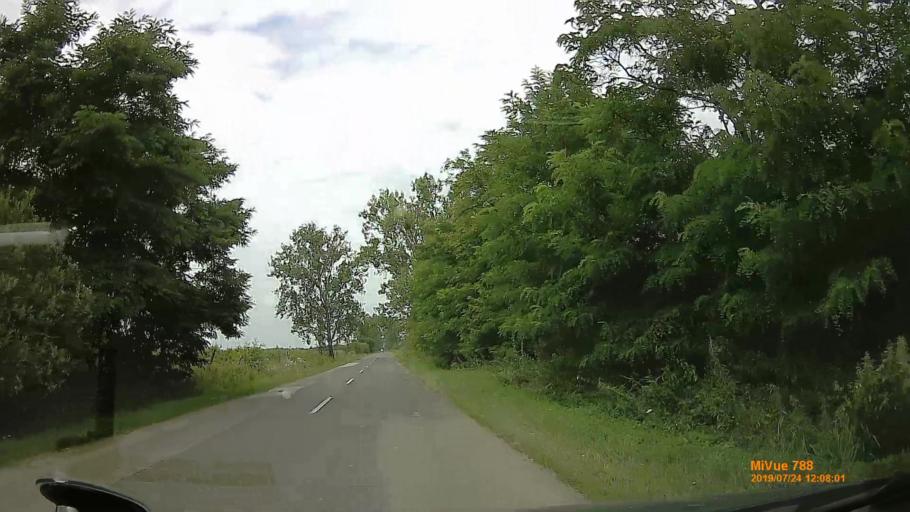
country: HU
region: Szabolcs-Szatmar-Bereg
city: Vasarosnameny
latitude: 48.1936
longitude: 22.3882
